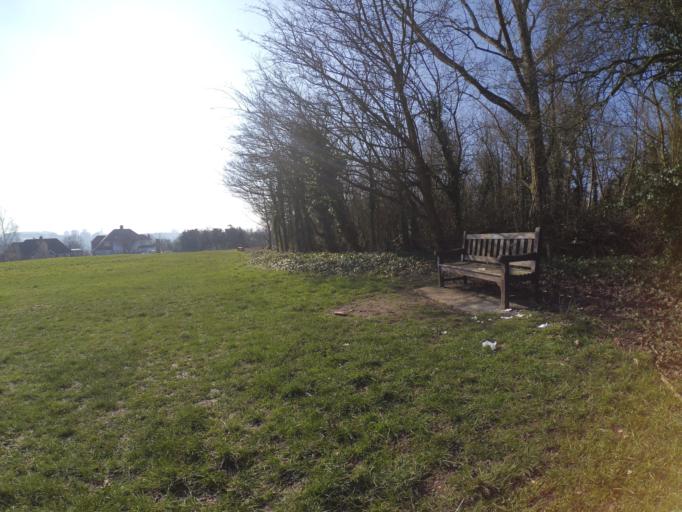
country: GB
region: England
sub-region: Greater London
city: Wembley
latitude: 51.5722
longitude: -0.2800
